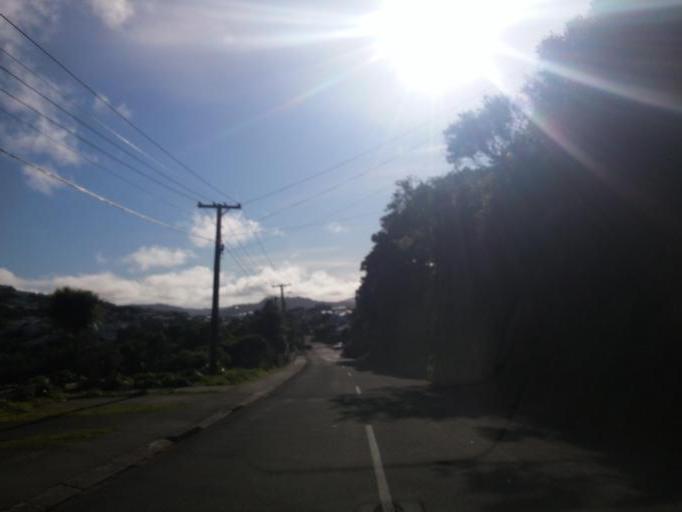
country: NZ
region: Wellington
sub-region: Wellington City
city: Brooklyn
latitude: -41.3098
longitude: 174.7643
